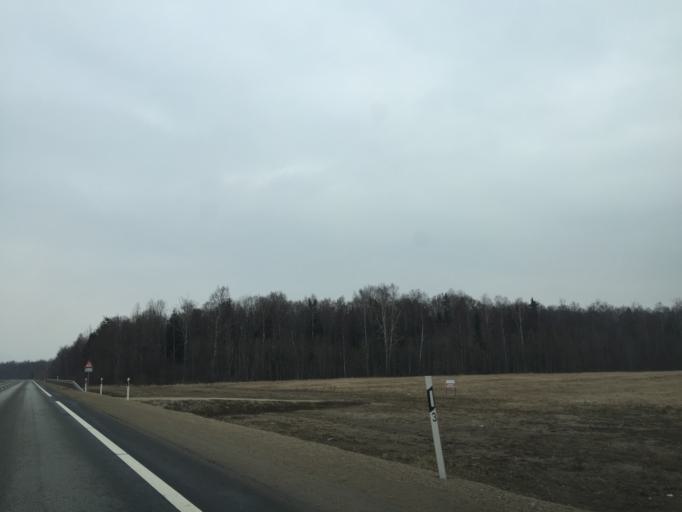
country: LV
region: Salacgrivas
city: Salacgriva
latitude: 57.7252
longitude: 24.3651
